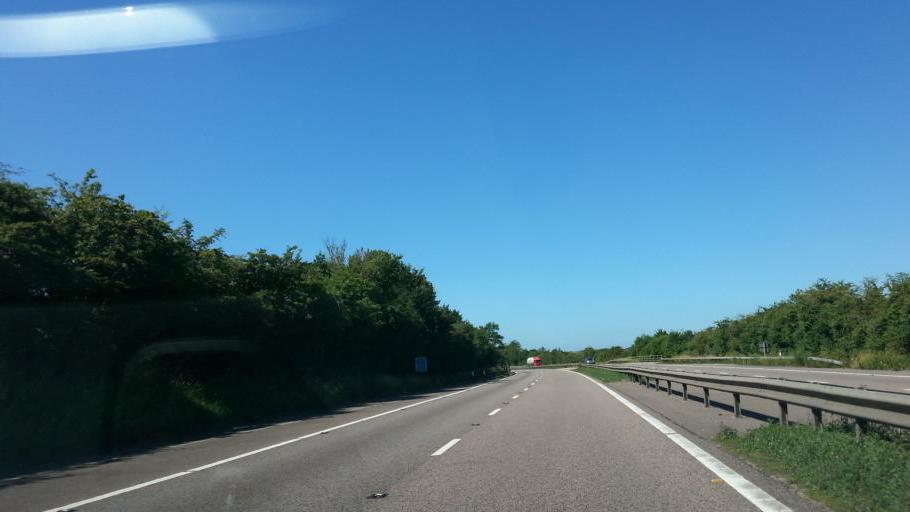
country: GB
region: England
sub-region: Worcestershire
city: Upton upon Severn
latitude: 52.0166
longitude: -2.2295
